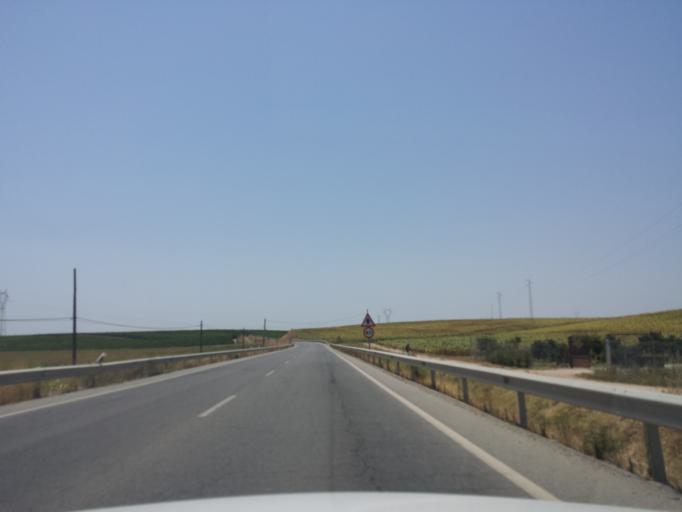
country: ES
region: Andalusia
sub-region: Provincia de Sevilla
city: Acala del Rio
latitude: 37.5347
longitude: -5.9578
